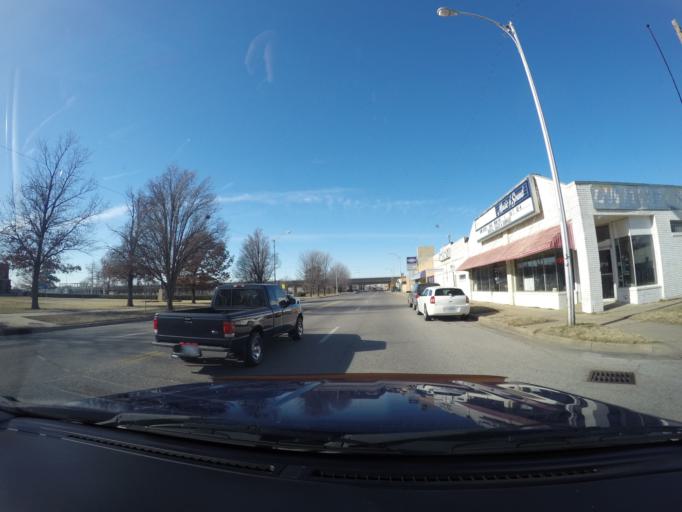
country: US
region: Kansas
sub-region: Sedgwick County
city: Wichita
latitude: 37.6862
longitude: -97.3108
